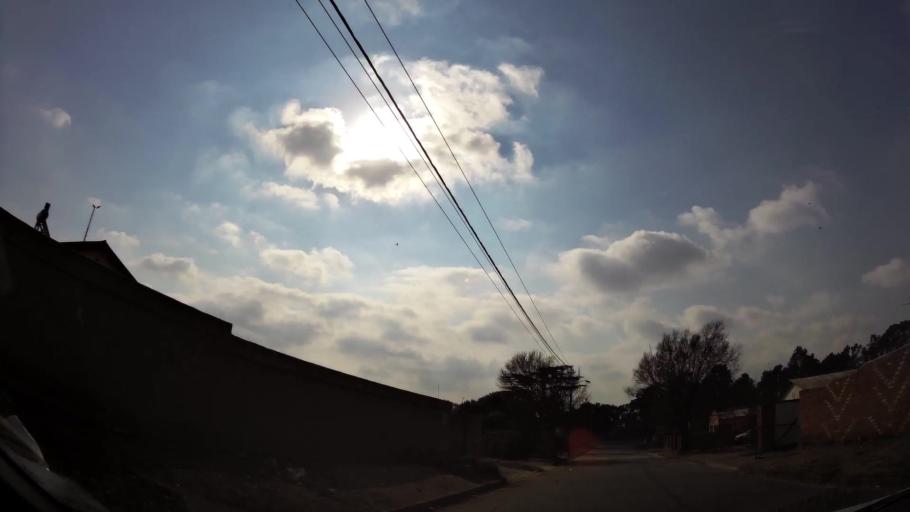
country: ZA
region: Gauteng
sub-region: City of Johannesburg Metropolitan Municipality
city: Modderfontein
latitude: -26.1559
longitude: 28.2036
